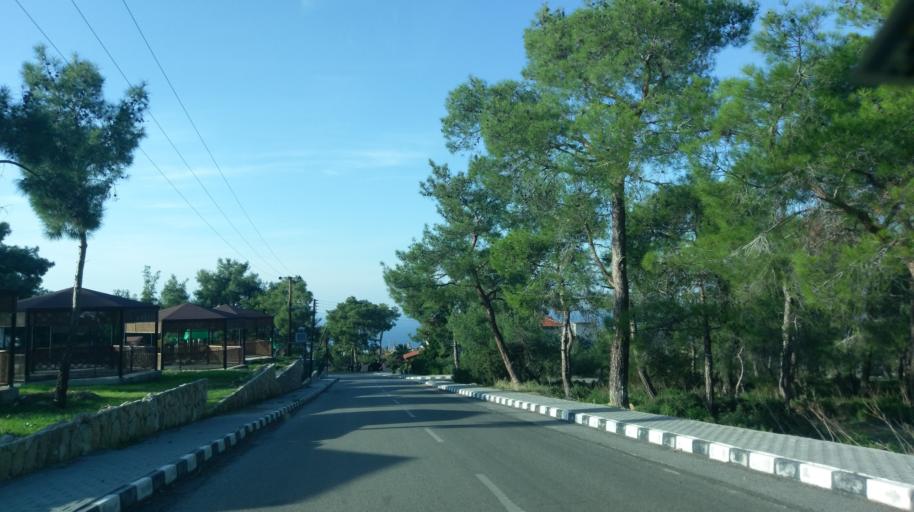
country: CY
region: Ammochostos
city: Lefkonoiko
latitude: 35.3338
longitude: 33.5861
